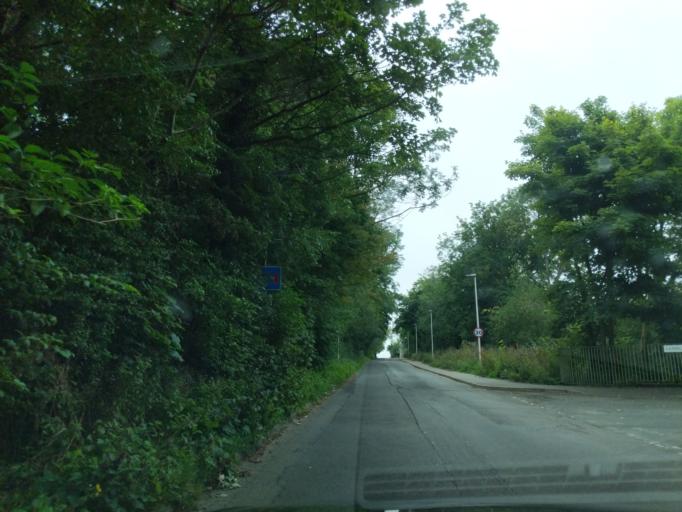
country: GB
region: Scotland
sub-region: East Lothian
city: Pencaitland
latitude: 55.9074
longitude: -2.8927
